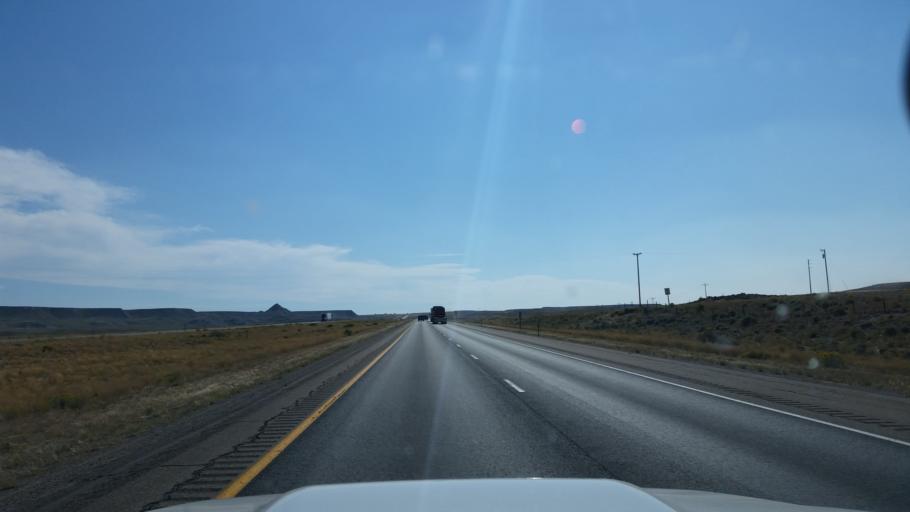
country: US
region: Wyoming
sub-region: Uinta County
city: Lyman
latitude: 41.5133
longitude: -109.9786
